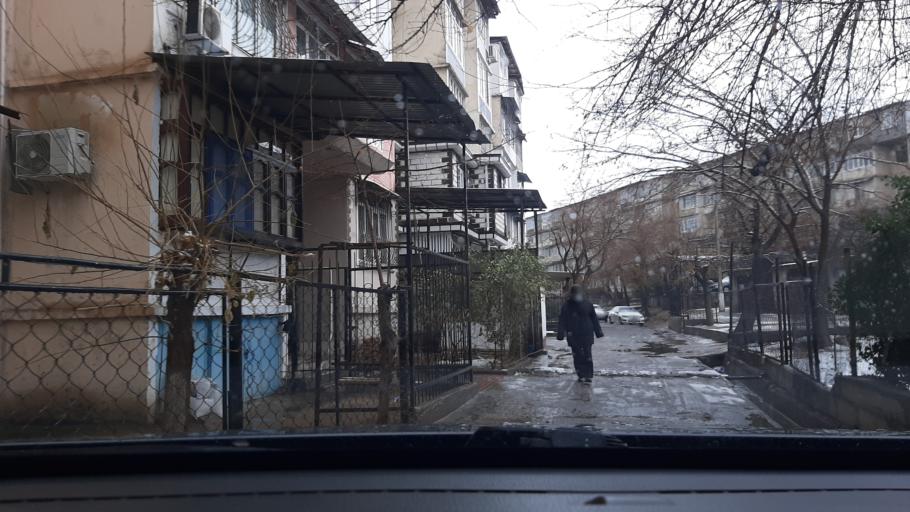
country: TJ
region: Viloyati Sughd
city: Khujand
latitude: 40.3000
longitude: 69.6076
